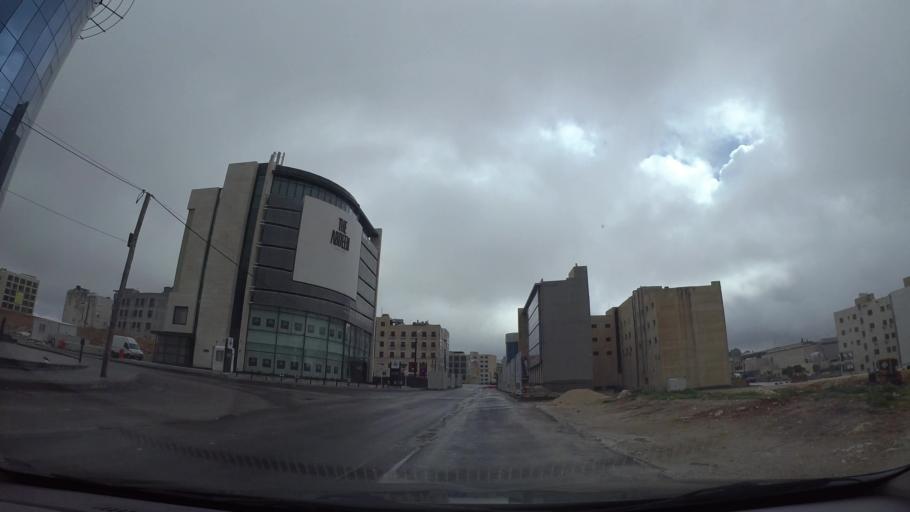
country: JO
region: Amman
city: Wadi as Sir
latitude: 31.9563
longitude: 35.8539
